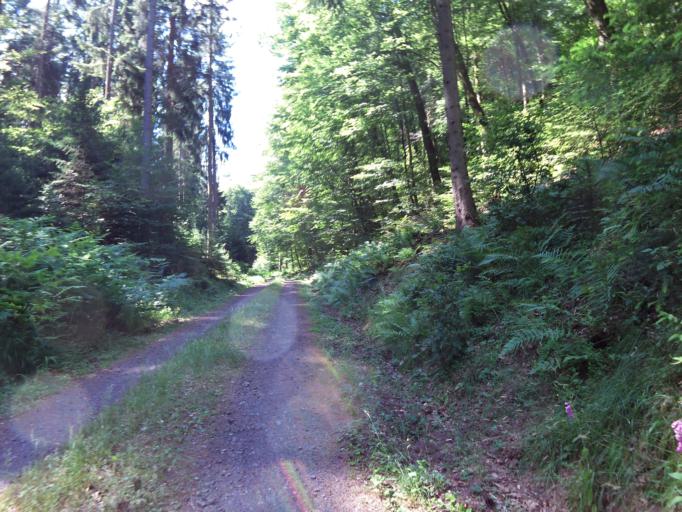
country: DE
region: Rheinland-Pfalz
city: Waldleiningen
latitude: 49.3903
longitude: 7.8637
